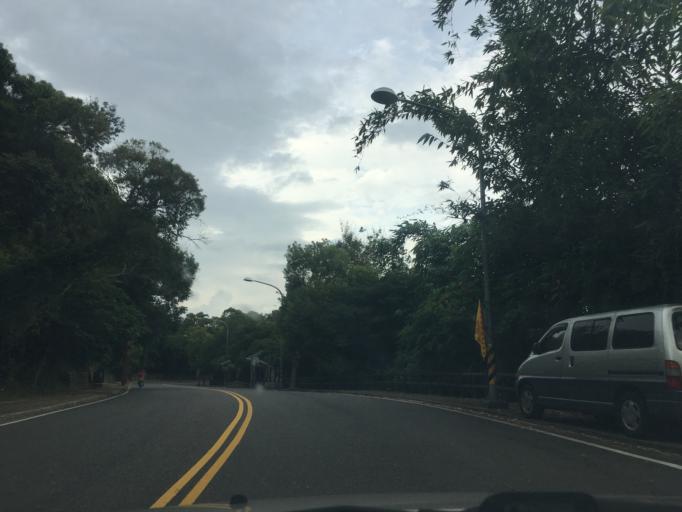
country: TW
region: Taiwan
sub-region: Changhua
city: Chang-hua
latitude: 24.0627
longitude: 120.5713
